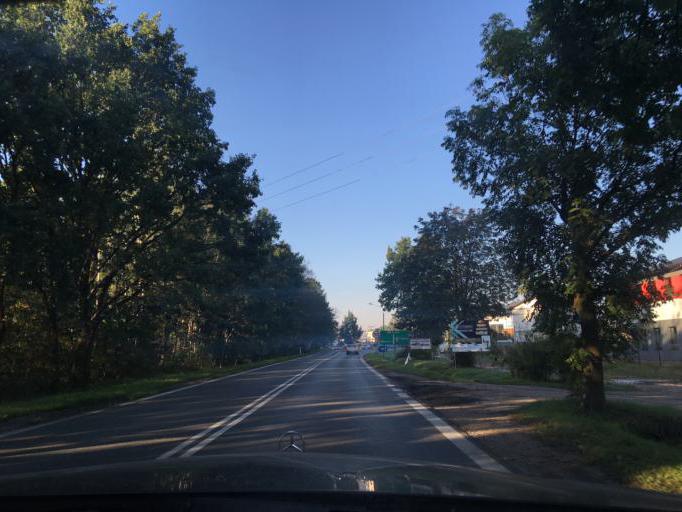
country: PL
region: Masovian Voivodeship
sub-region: Powiat pruszkowski
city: Otrebusy
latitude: 52.1322
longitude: 20.7588
